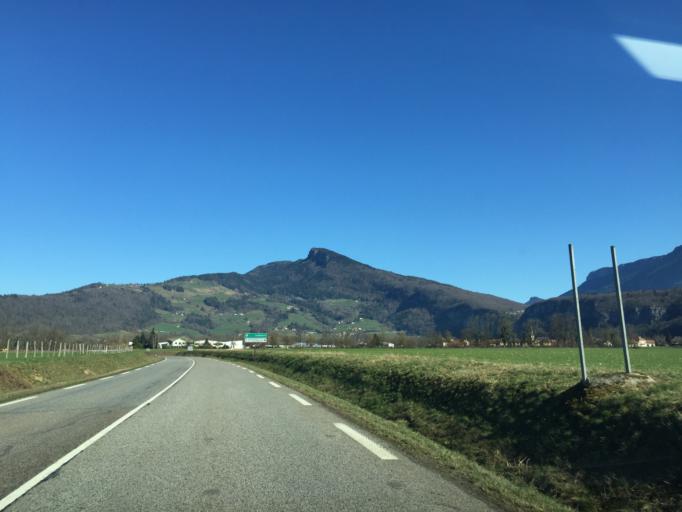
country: FR
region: Rhone-Alpes
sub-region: Departement de la Savoie
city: Les Echelles
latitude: 45.4326
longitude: 5.7651
